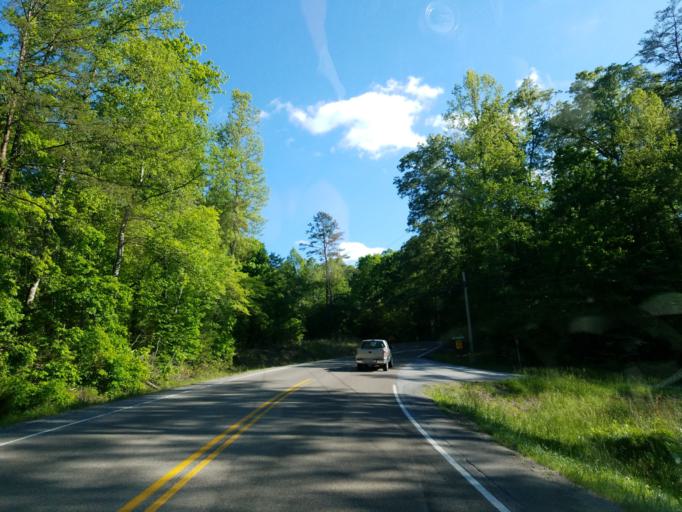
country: US
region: Georgia
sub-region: Fannin County
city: Blue Ridge
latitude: 34.8627
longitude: -84.2301
